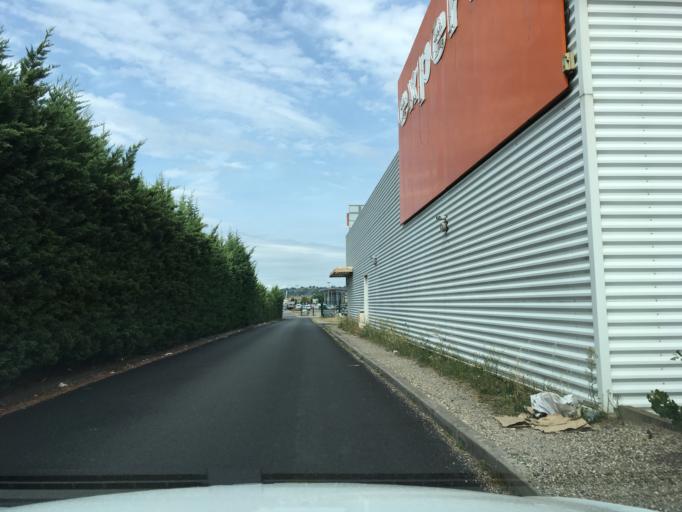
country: FR
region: Aquitaine
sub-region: Departement du Lot-et-Garonne
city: Boe
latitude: 44.1793
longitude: 0.6199
